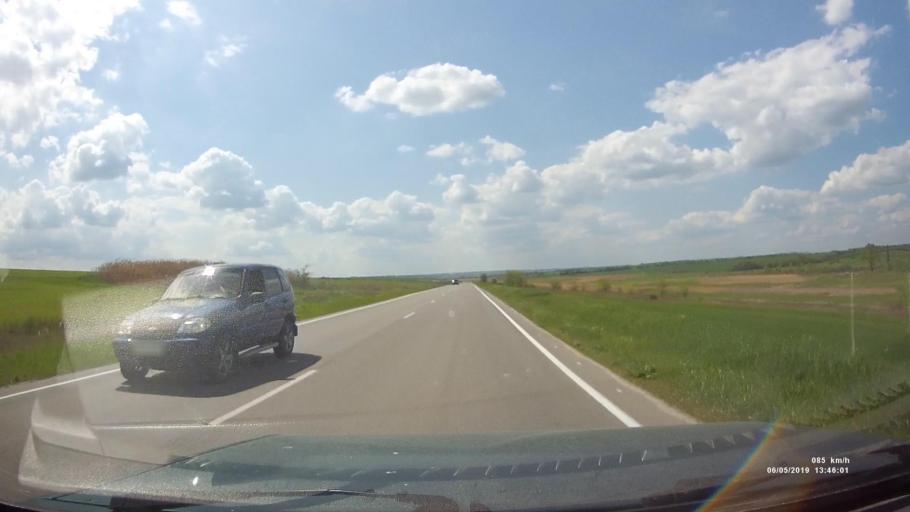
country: RU
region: Rostov
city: Melikhovskaya
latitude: 47.6576
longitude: 40.5896
